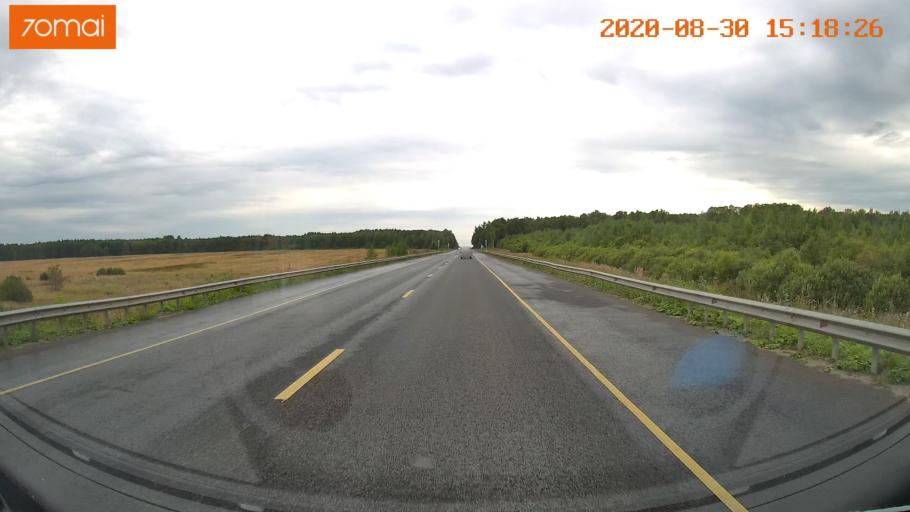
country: RU
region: Ivanovo
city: Rodniki
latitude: 57.1232
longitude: 41.7937
